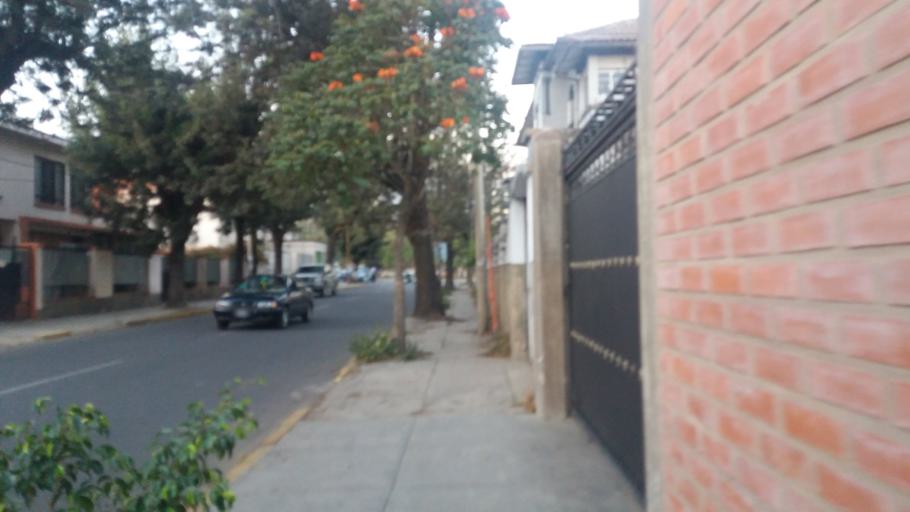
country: BO
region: Cochabamba
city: Cochabamba
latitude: -17.3851
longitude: -66.1542
